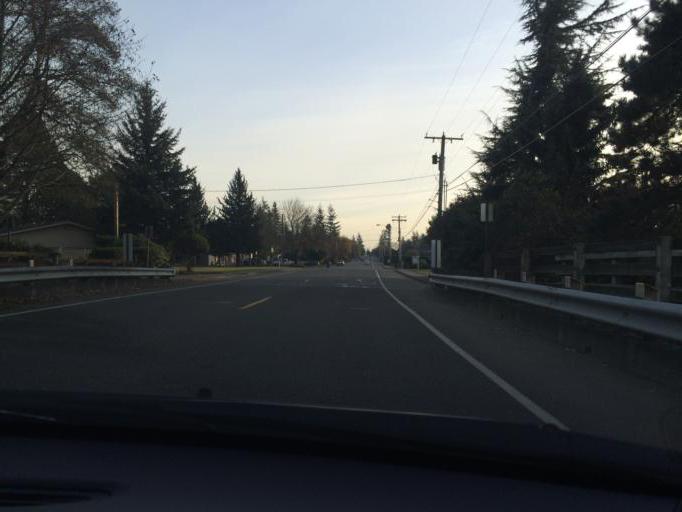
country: US
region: Washington
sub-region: Whatcom County
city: Lynden
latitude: 48.9556
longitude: -122.4412
